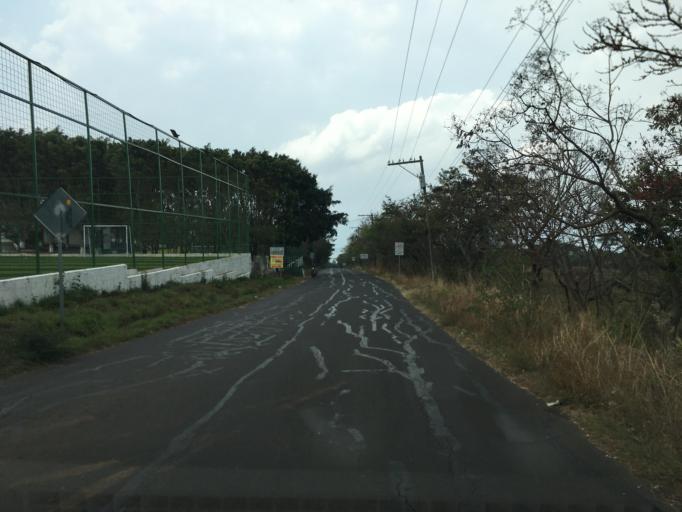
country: GT
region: Escuintla
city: San Vicente Pacaya
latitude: 14.3288
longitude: -90.5642
